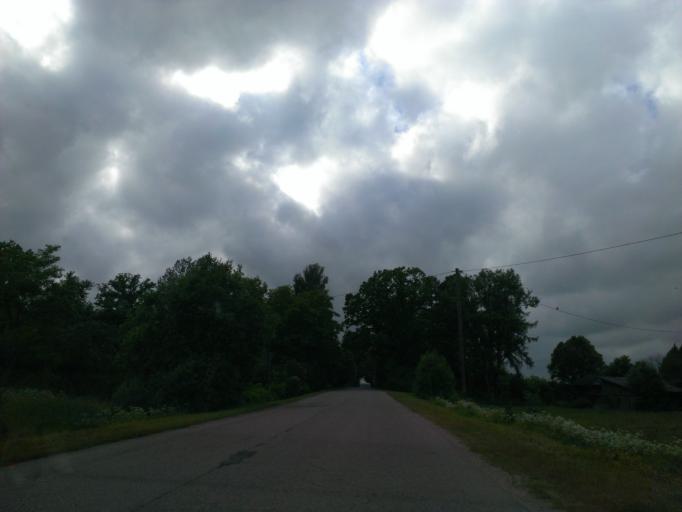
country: LV
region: Aizpute
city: Aizpute
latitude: 56.7123
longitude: 21.4797
